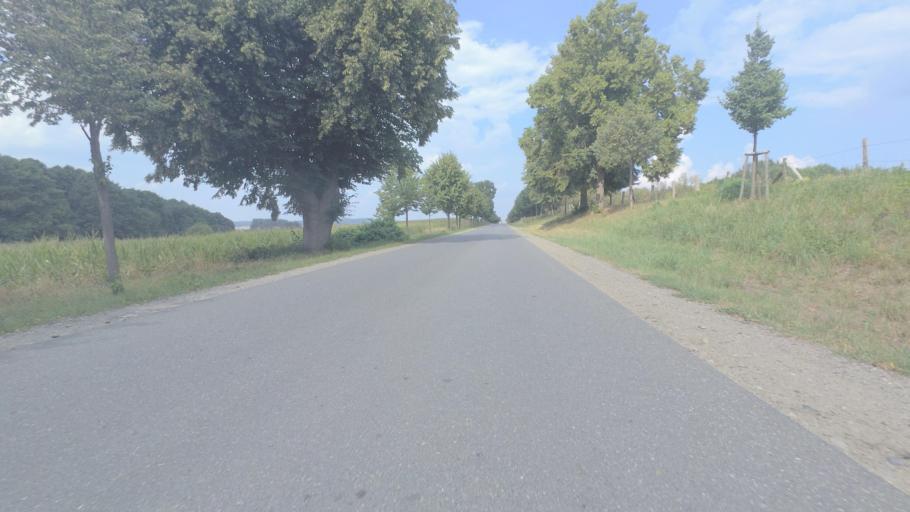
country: DE
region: Mecklenburg-Vorpommern
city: Malchin
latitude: 53.7635
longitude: 12.8345
